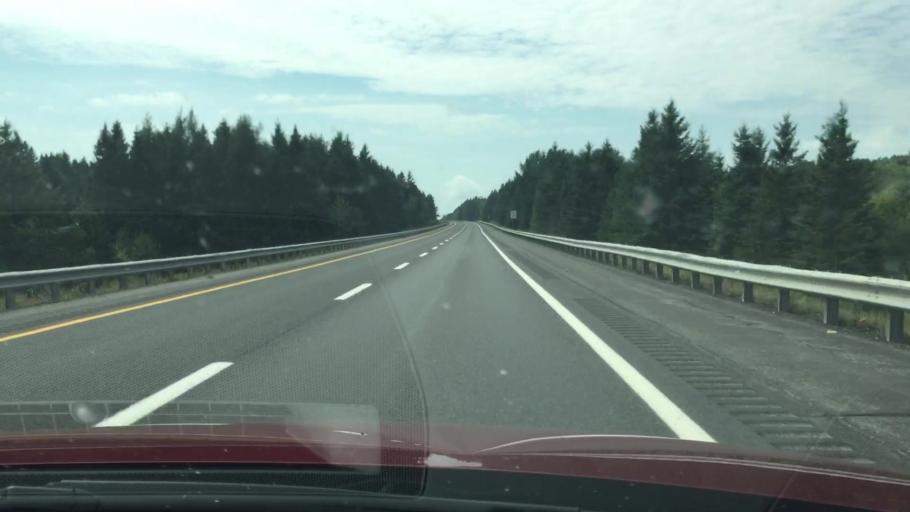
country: US
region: Maine
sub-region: Aroostook County
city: Hodgdon
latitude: 46.1382
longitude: -68.0776
